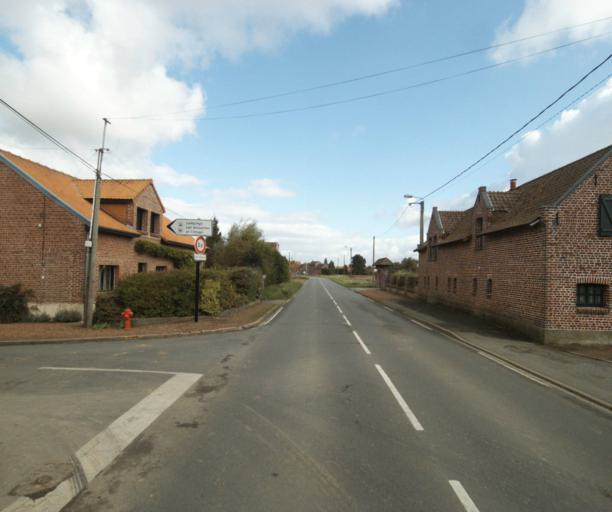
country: FR
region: Nord-Pas-de-Calais
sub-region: Departement du Nord
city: Perenchies
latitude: 50.6761
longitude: 2.9540
